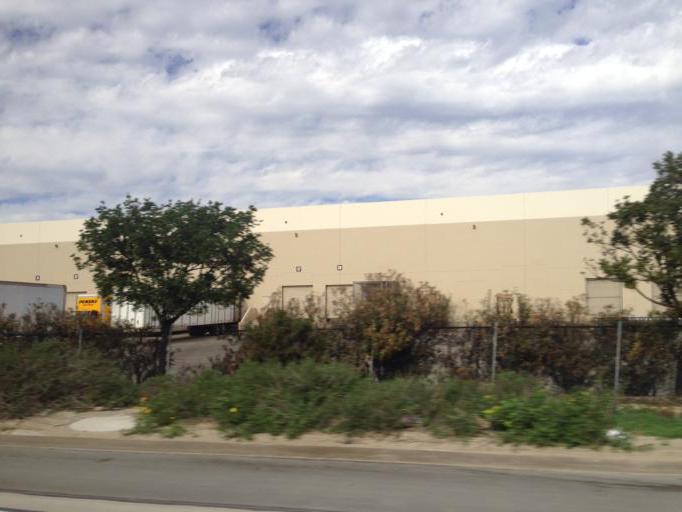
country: MX
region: Baja California
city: Tijuana
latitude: 32.5644
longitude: -116.9732
